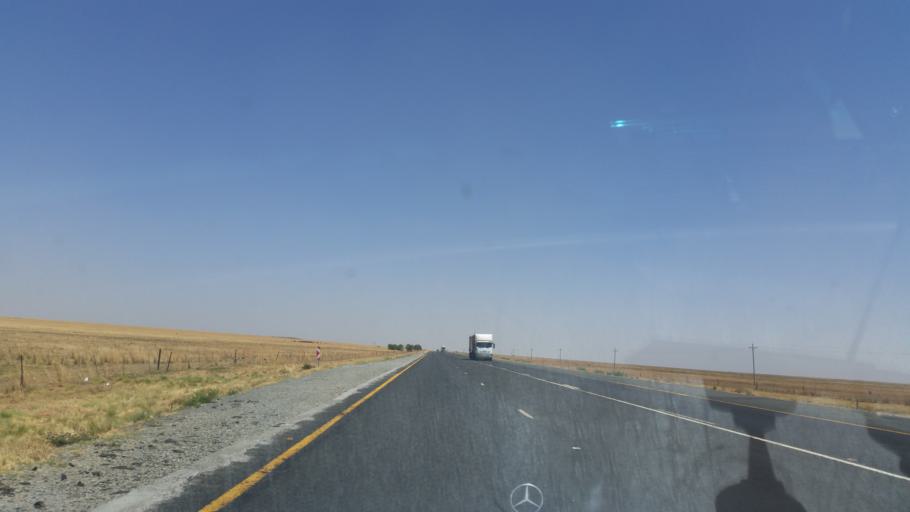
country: ZA
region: Orange Free State
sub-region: Lejweleputswa District Municipality
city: Brandfort
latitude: -28.8026
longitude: 26.6855
